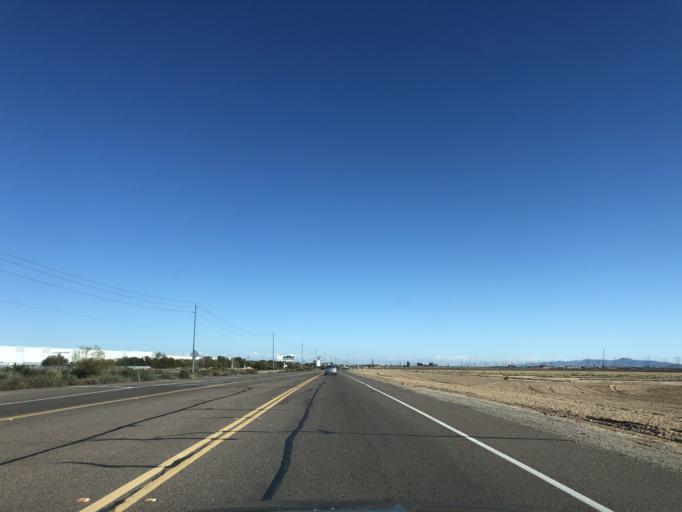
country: US
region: Arizona
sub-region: Maricopa County
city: Goodyear
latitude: 33.4047
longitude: -112.4239
